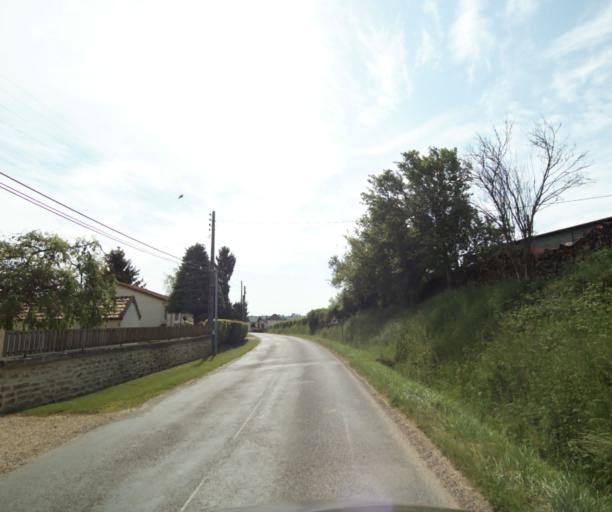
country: FR
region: Bourgogne
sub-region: Departement de Saone-et-Loire
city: Paray-le-Monial
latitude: 46.5377
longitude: 4.1262
